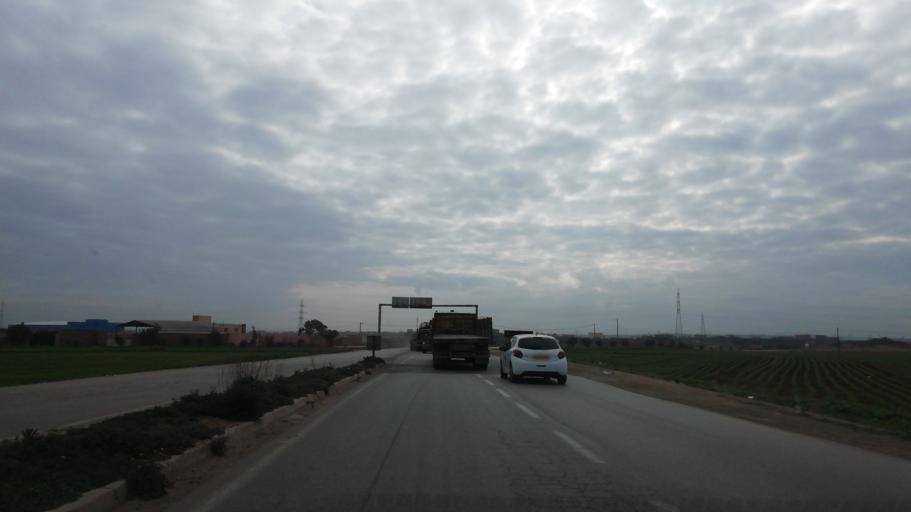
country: DZ
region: Oran
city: Ain el Bya
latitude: 35.7951
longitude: -0.3431
